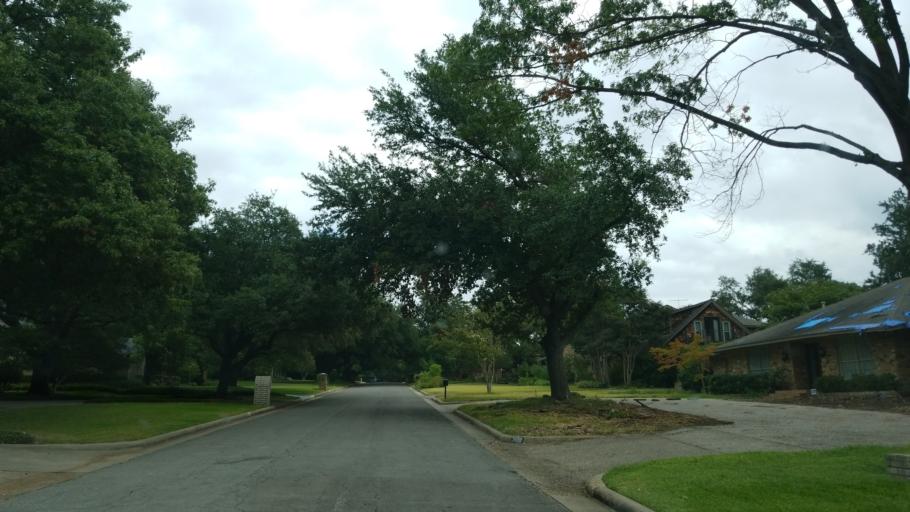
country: US
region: Texas
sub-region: Dallas County
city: Richardson
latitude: 32.9431
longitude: -96.7765
